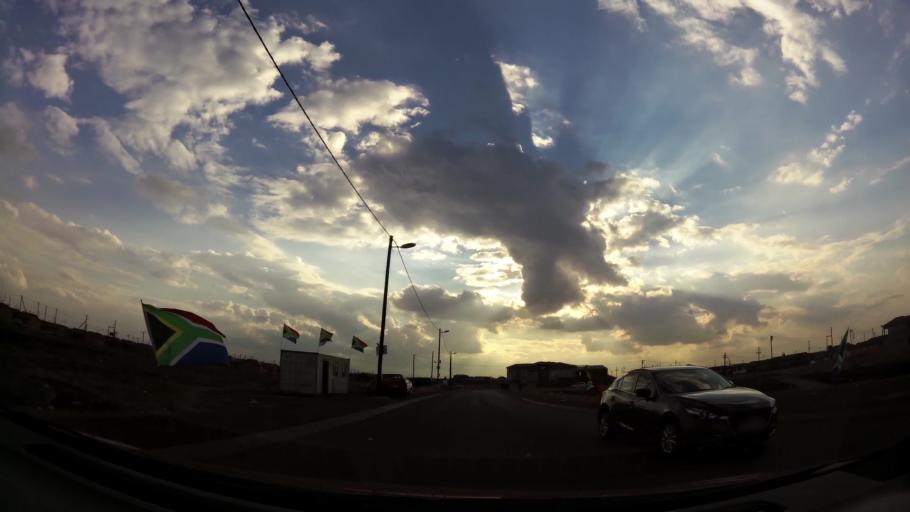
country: ZA
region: Gauteng
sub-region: Sedibeng District Municipality
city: Vanderbijlpark
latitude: -26.6141
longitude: 27.8133
